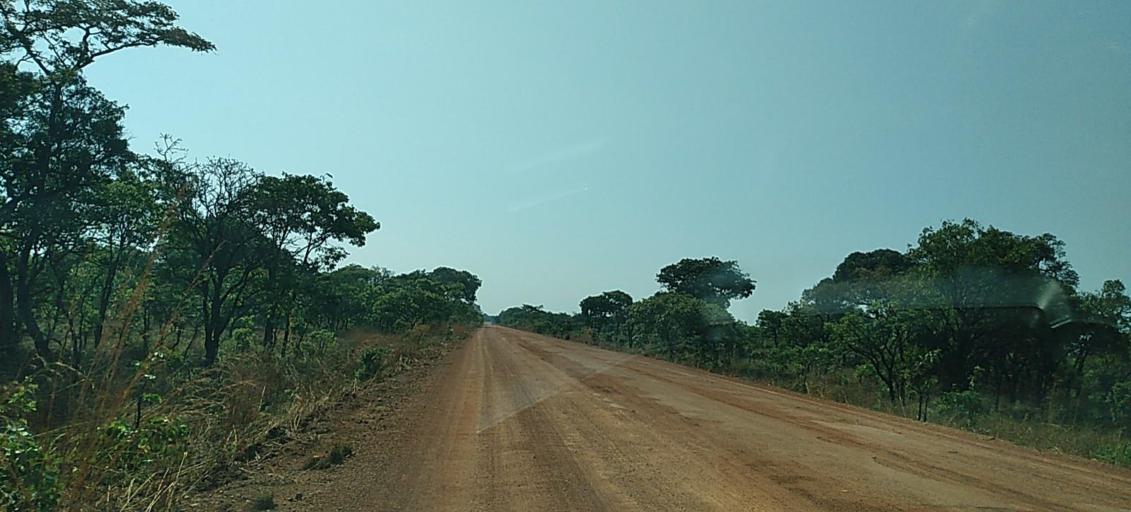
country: ZM
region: North-Western
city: Mwinilunga
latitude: -11.9139
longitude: 25.3039
